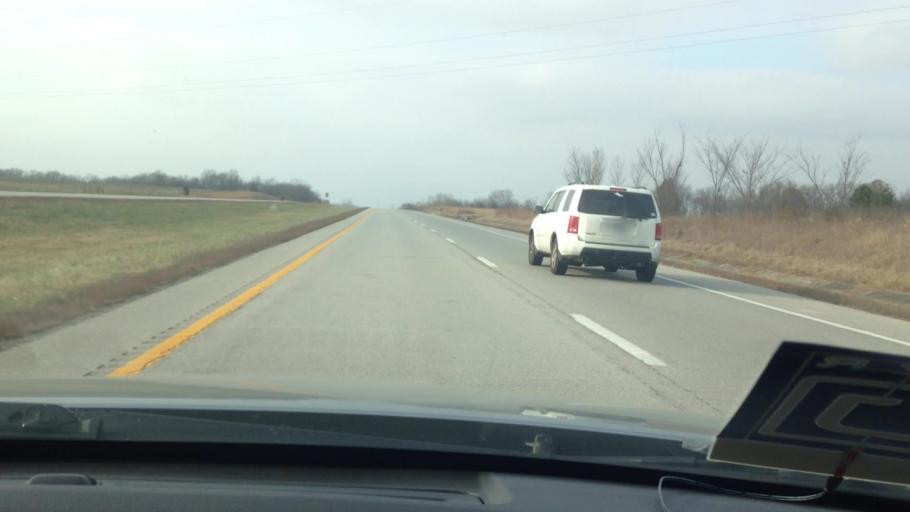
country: US
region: Missouri
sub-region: Cass County
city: Garden City
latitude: 38.5299
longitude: -94.1496
